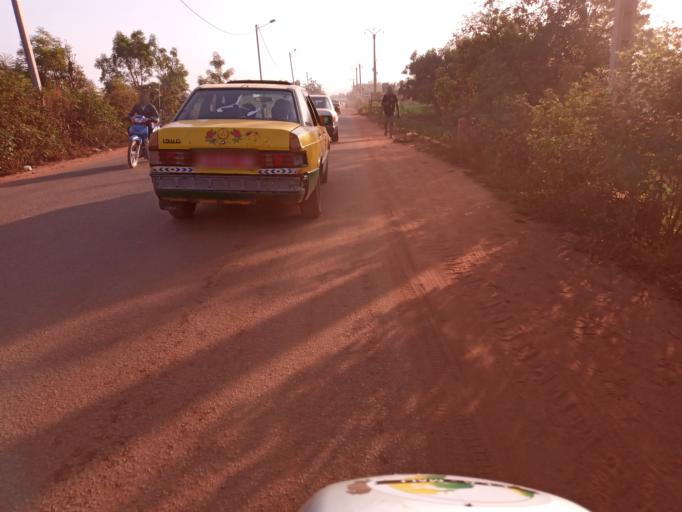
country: ML
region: Bamako
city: Bamako
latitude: 12.6357
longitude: -7.9290
